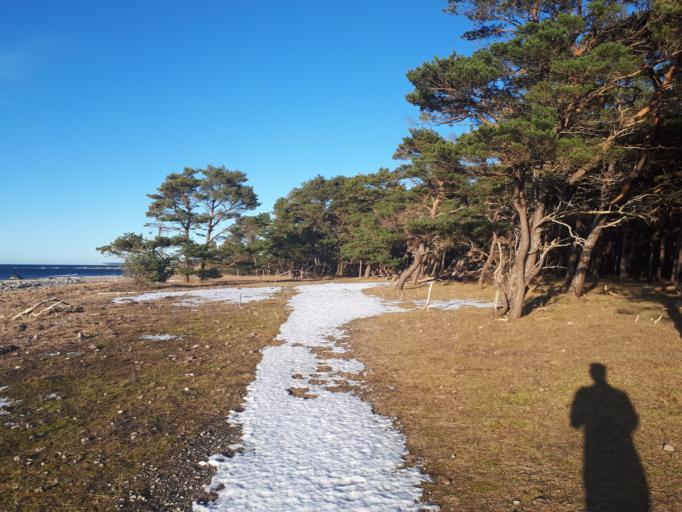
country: SE
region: Gotland
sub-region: Gotland
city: Visby
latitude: 57.6879
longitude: 18.3462
